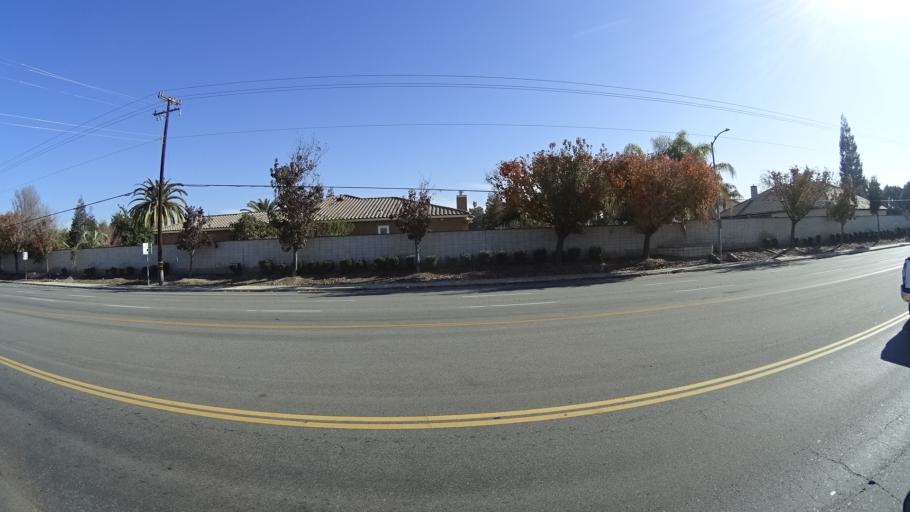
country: US
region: California
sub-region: Kern County
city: Rosedale
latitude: 35.3678
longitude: -119.1456
